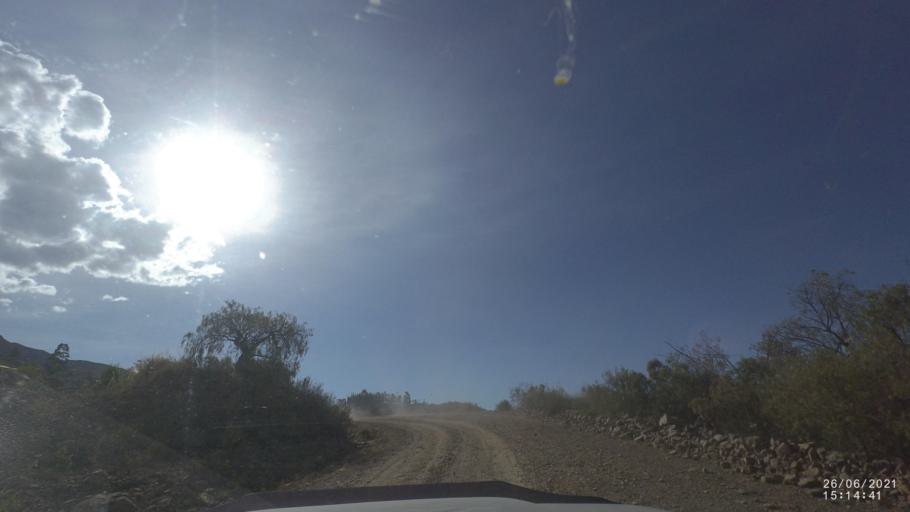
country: BO
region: Cochabamba
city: Mizque
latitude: -17.9608
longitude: -65.6437
